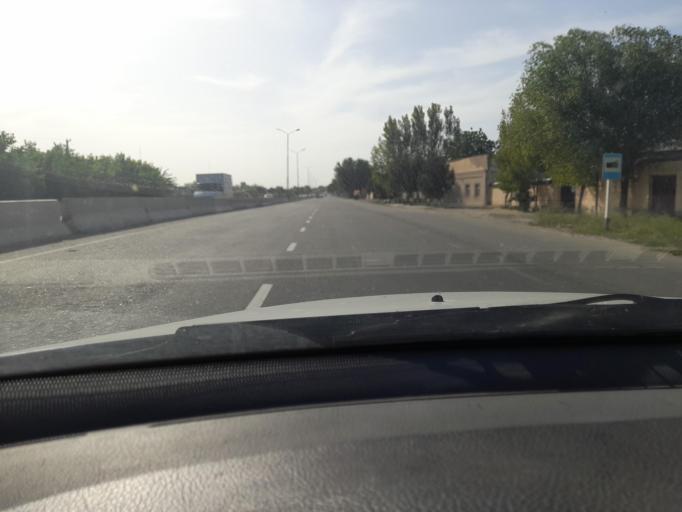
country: UZ
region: Samarqand
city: Kattaqo'rg'on
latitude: 39.9246
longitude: 66.2254
